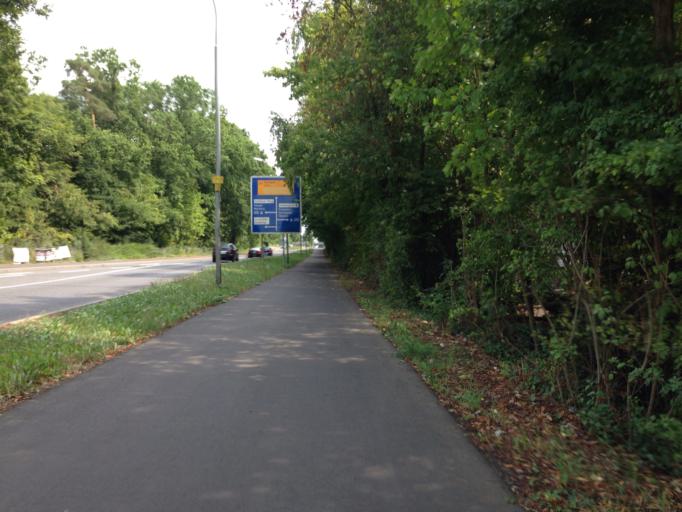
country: DE
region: Hesse
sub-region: Regierungsbezirk Giessen
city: Giessen
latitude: 50.5795
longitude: 8.7014
